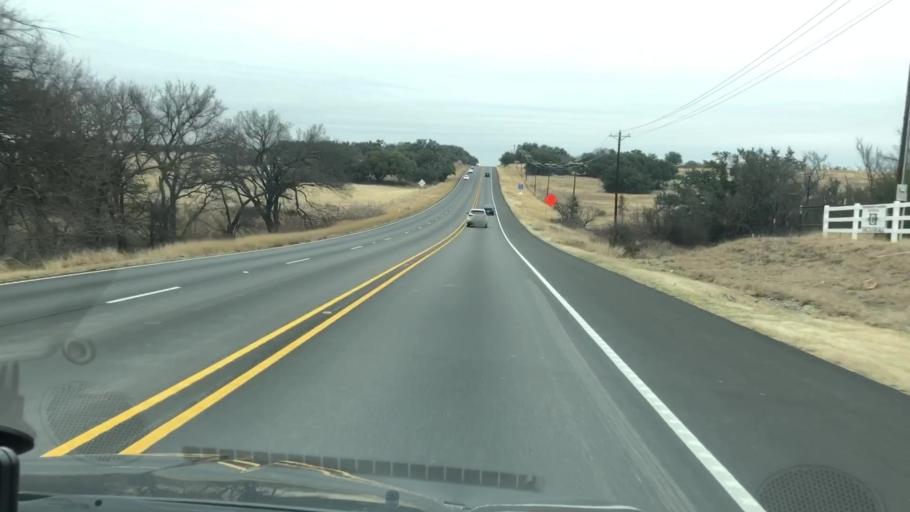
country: US
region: Texas
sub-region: Erath County
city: Stephenville
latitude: 32.3013
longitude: -98.1875
